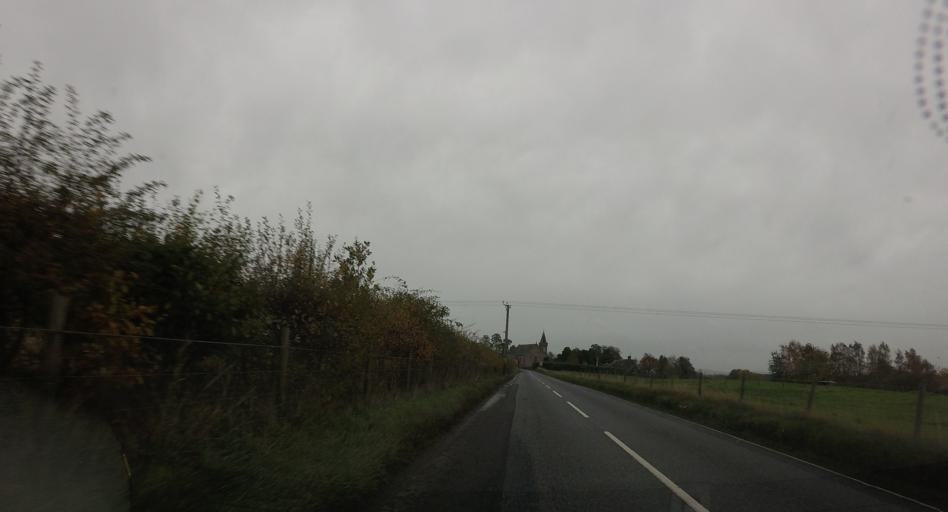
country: GB
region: Scotland
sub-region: Perth and Kinross
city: Bankfoot
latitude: 56.5441
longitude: -3.4892
